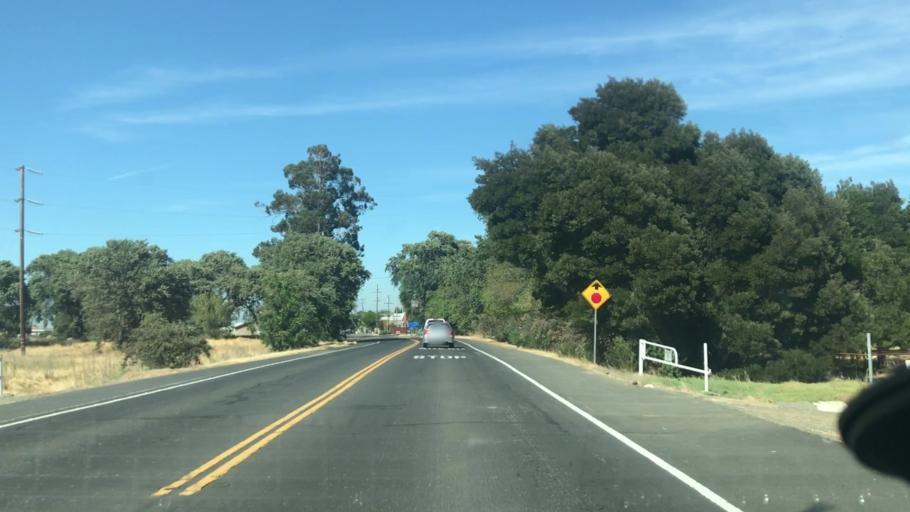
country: US
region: California
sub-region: Solano County
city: Vacaville
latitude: 38.3473
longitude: -121.9115
